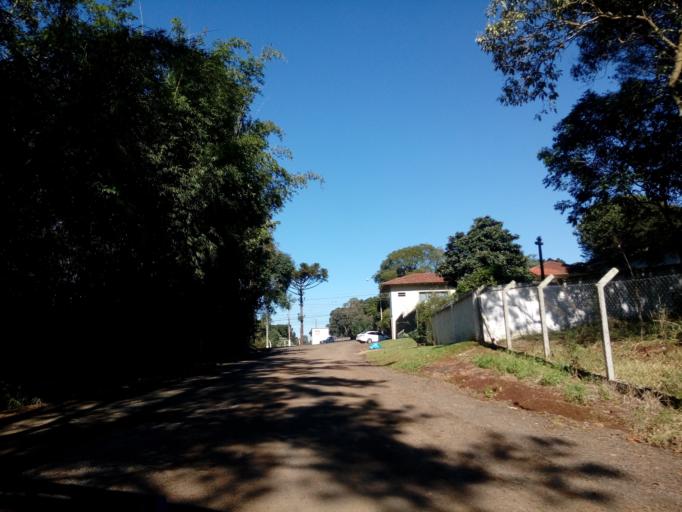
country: BR
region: Santa Catarina
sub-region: Chapeco
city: Chapeco
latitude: -27.0963
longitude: -52.6578
